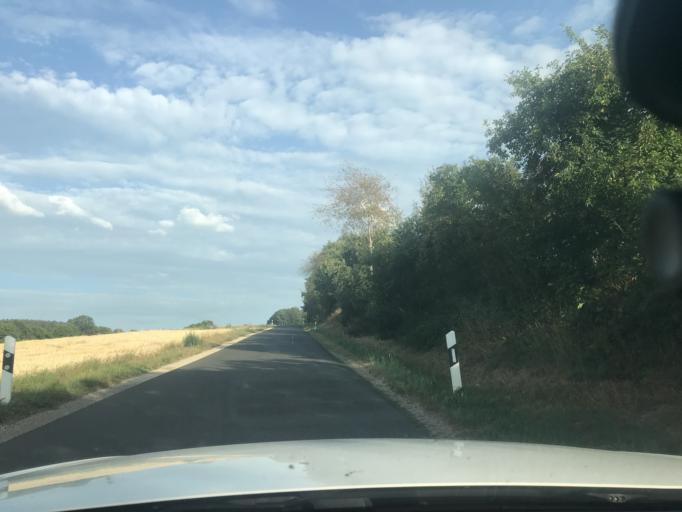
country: DE
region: Bavaria
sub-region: Upper Franconia
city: Pegnitz
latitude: 49.7780
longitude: 11.5815
